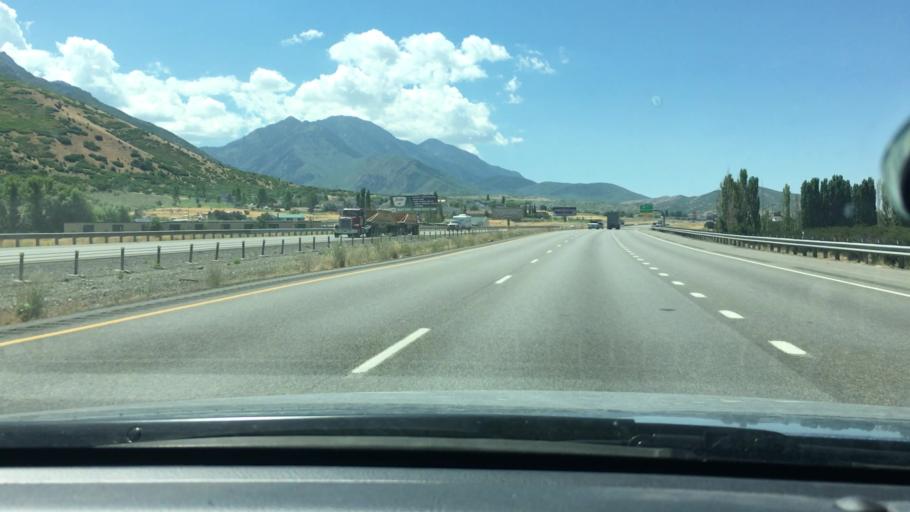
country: US
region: Utah
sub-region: Utah County
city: Santaquin
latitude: 39.9887
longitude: -111.7646
